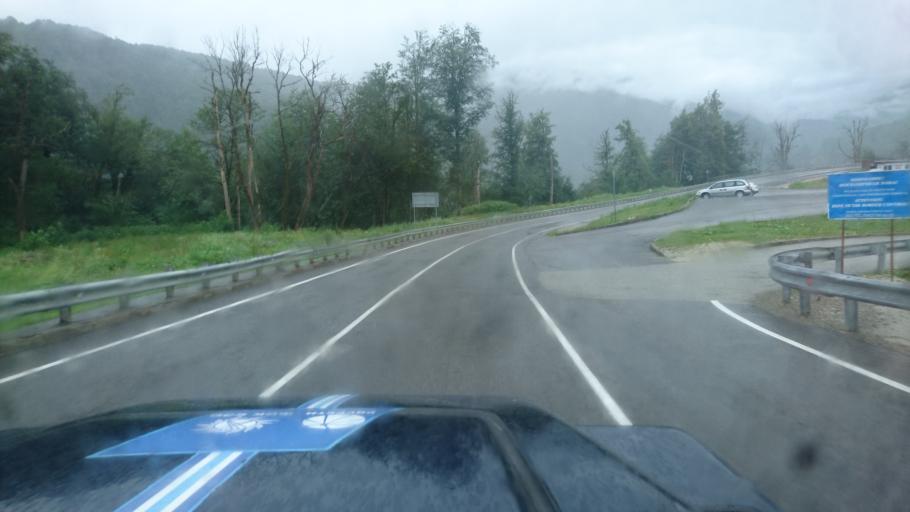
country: RU
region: Krasnodarskiy
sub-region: Sochi City
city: Krasnaya Polyana
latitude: 43.6487
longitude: 40.3382
